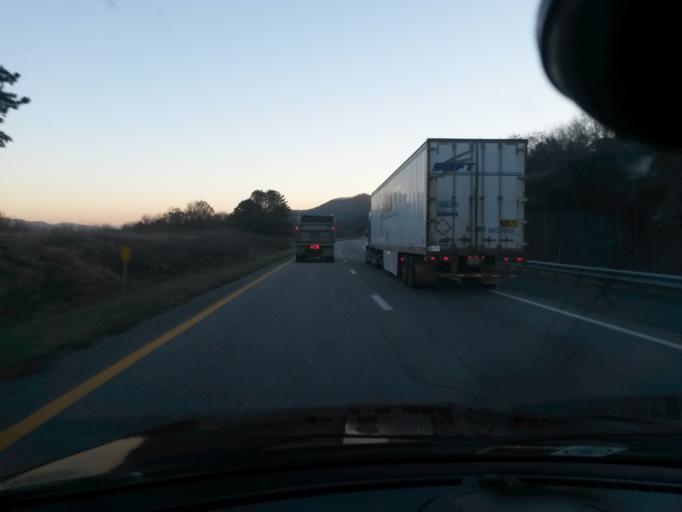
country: US
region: Virginia
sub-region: City of Lexington
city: Lexington
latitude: 37.8854
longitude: -79.5989
